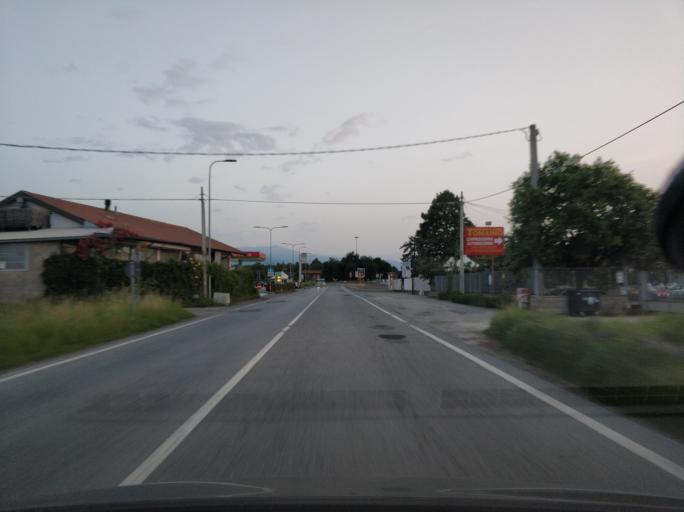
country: IT
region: Piedmont
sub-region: Provincia di Torino
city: San Maurizio
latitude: 45.2032
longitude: 7.6372
